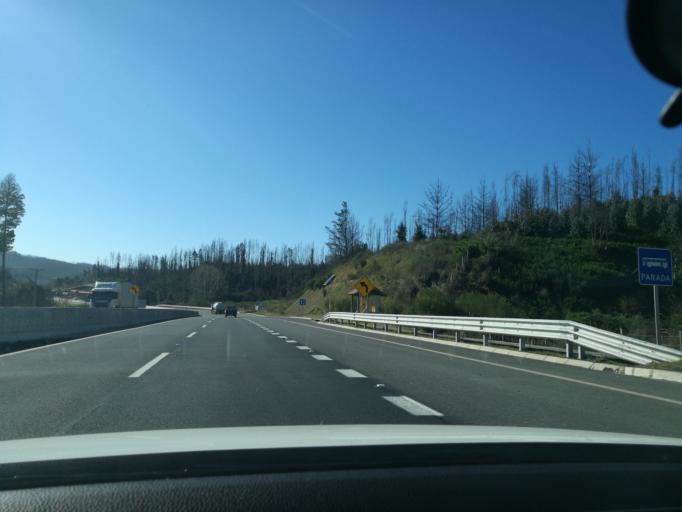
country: CL
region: Biobio
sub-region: Provincia de Concepcion
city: Chiguayante
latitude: -36.8571
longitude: -72.8851
